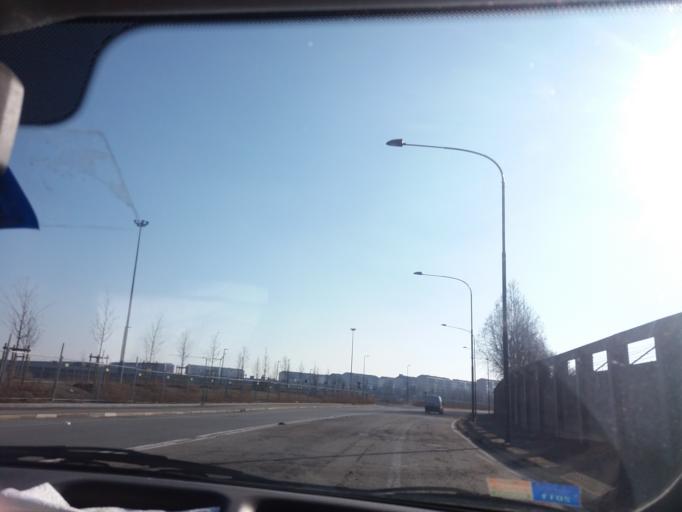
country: IT
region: Piedmont
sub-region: Provincia di Torino
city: Fornaci
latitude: 45.0279
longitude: 7.6090
